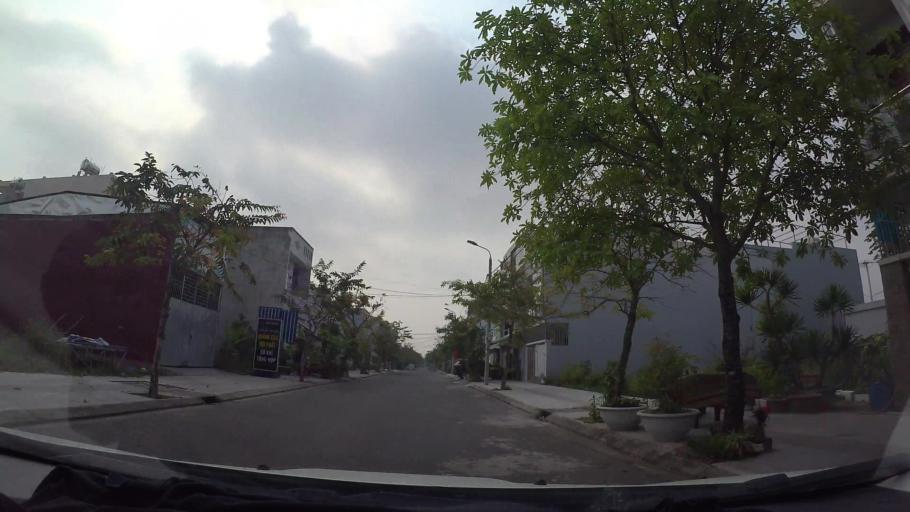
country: VN
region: Da Nang
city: Cam Le
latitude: 16.0097
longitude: 108.2167
